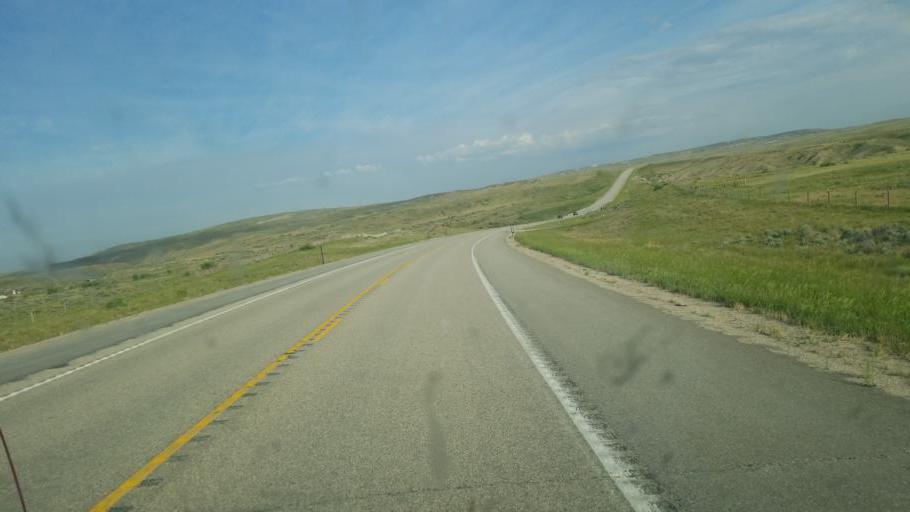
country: US
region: Wyoming
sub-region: Natrona County
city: Mills
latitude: 43.0338
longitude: -107.0139
